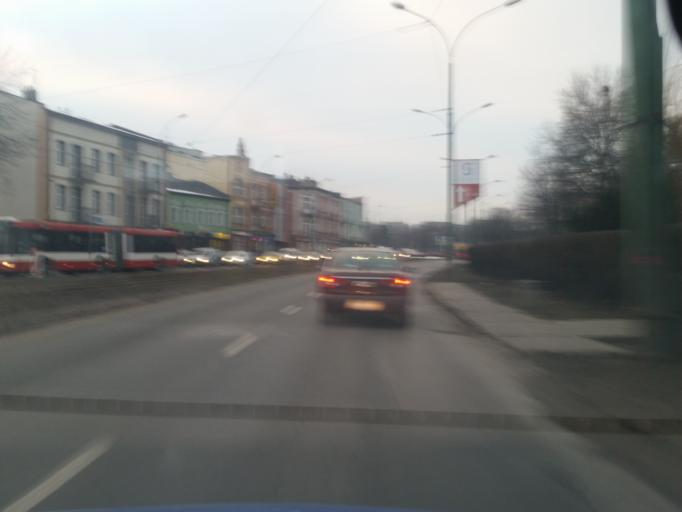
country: PL
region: Silesian Voivodeship
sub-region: Sosnowiec
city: Sosnowiec
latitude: 50.2776
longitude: 19.1193
